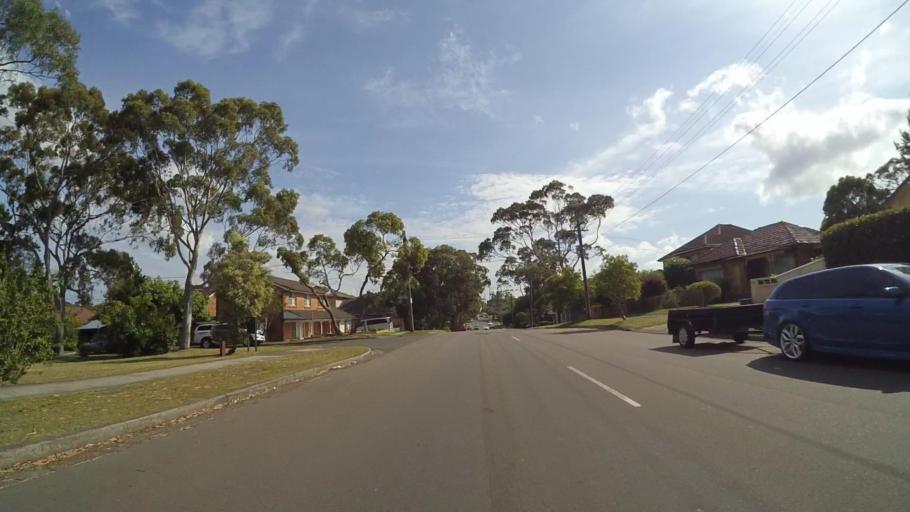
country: AU
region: New South Wales
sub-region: Sutherland Shire
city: Caringbah
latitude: -34.0482
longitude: 151.1171
